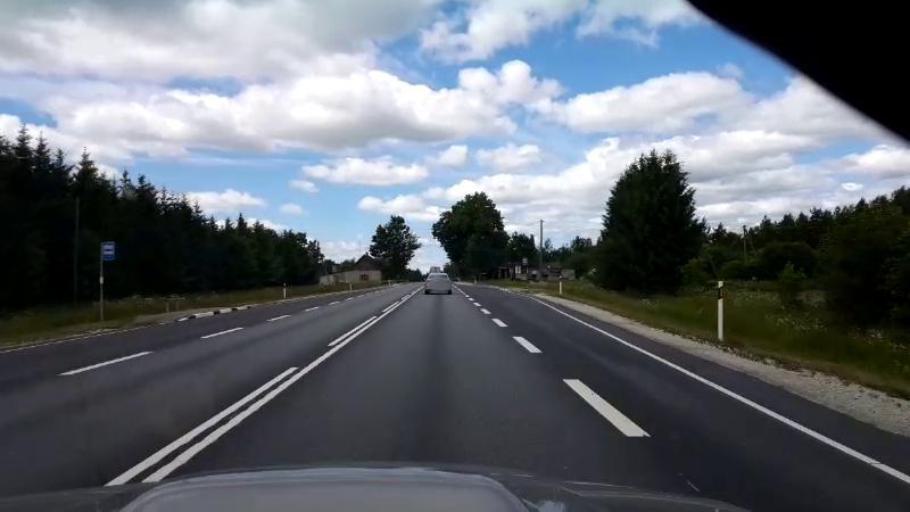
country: EE
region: Paernumaa
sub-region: Halinga vald
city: Parnu-Jaagupi
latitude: 58.6698
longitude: 24.4515
